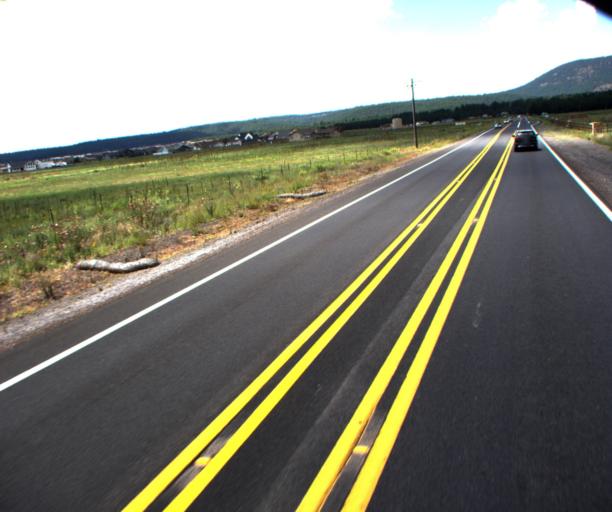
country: US
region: Arizona
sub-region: Coconino County
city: Flagstaff
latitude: 35.2683
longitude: -111.7249
